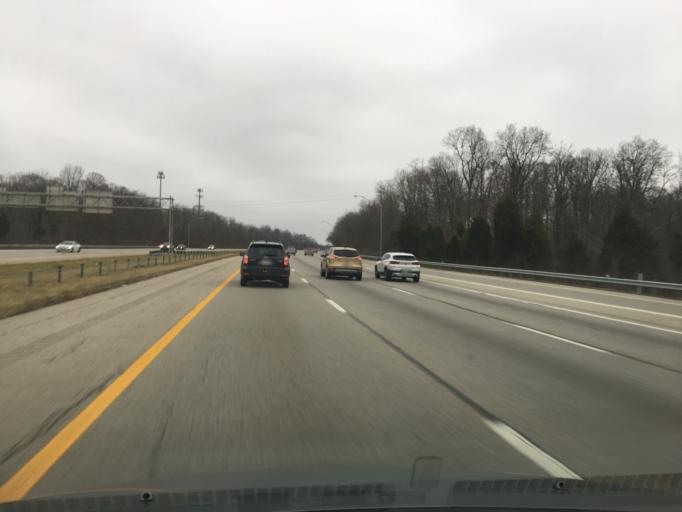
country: US
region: Ohio
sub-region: Hamilton County
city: The Village of Indian Hill
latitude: 39.2242
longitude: -84.2773
